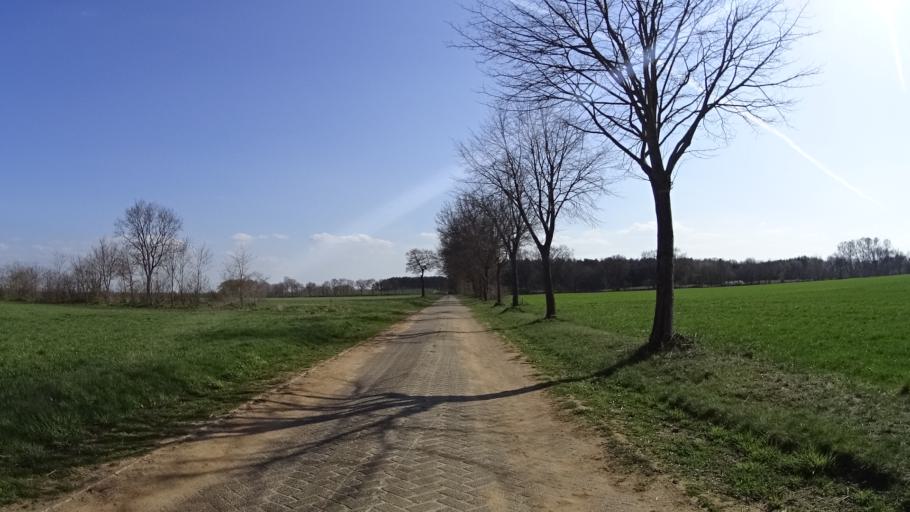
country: DE
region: Lower Saxony
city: Lehe
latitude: 52.9961
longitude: 7.3224
